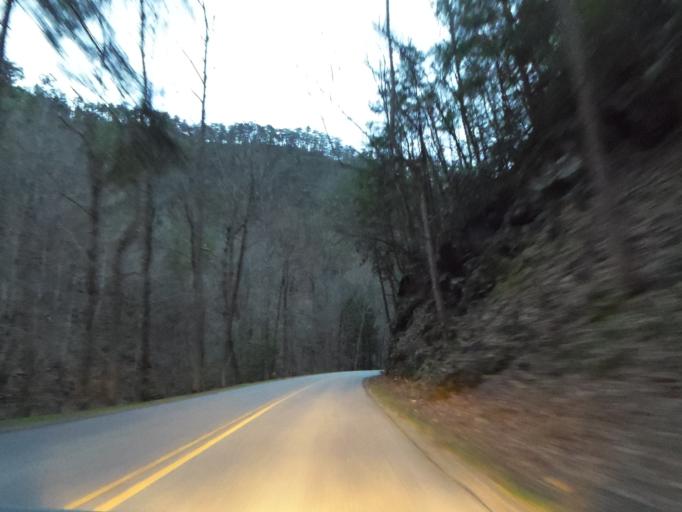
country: US
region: Tennessee
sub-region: Sevier County
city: Pigeon Forge
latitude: 35.6512
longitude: -83.7145
